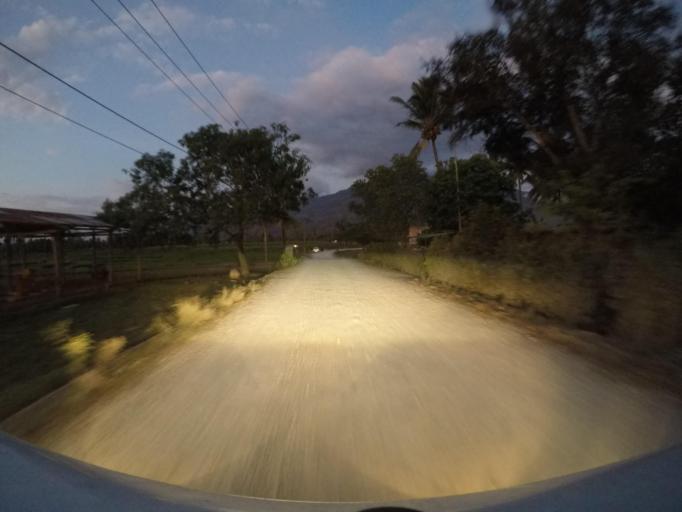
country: TL
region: Bobonaro
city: Maliana
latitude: -8.9812
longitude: 125.2139
